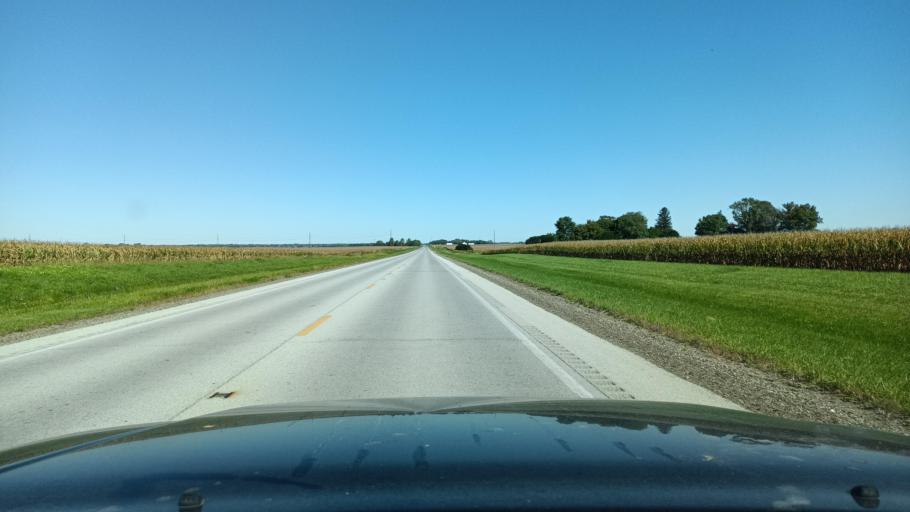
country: US
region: Illinois
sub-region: Champaign County
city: Philo
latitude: 40.0474
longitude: -88.1617
